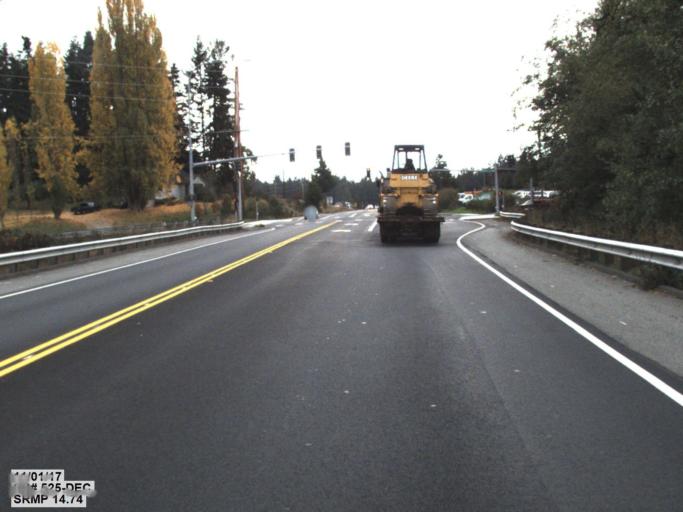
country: US
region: Washington
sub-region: Island County
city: Freeland
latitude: 48.0051
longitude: -122.4623
